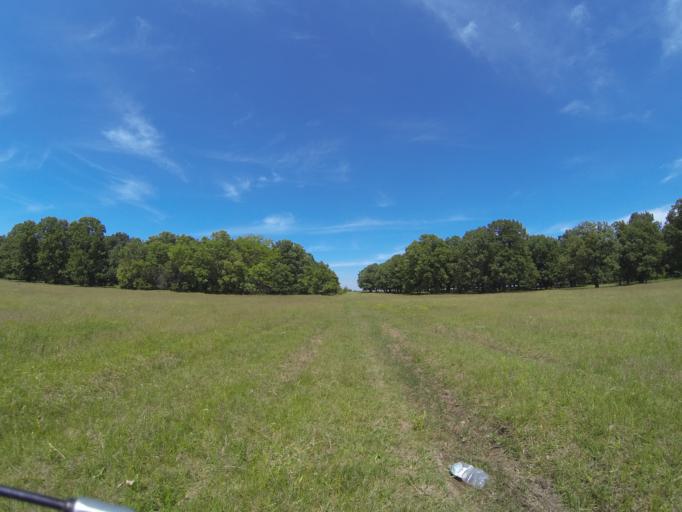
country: RO
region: Dolj
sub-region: Comuna Teslui
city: Teslui
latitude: 44.1731
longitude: 24.1666
